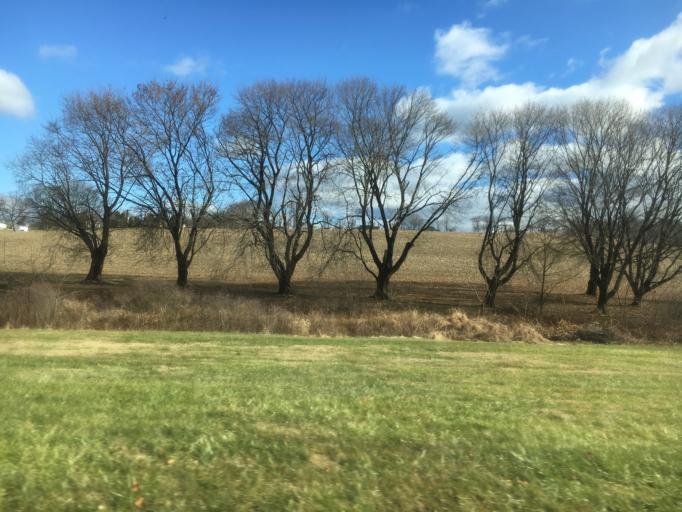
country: US
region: Pennsylvania
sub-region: Lehigh County
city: Egypt
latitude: 40.6997
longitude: -75.5696
